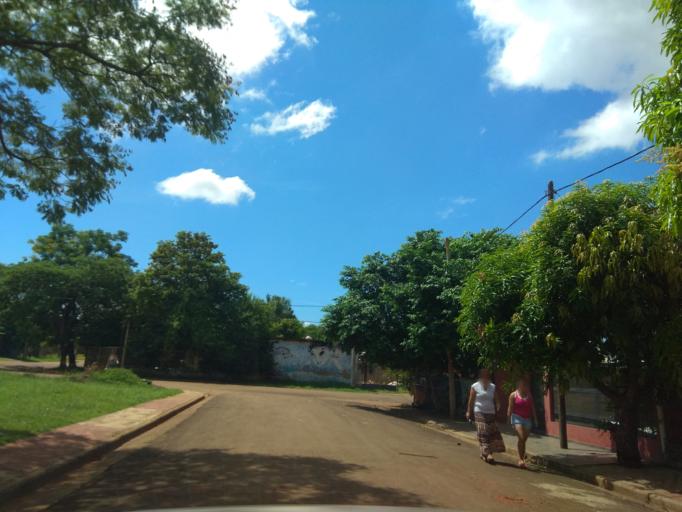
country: AR
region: Misiones
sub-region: Departamento de Capital
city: Posadas
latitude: -27.3861
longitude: -55.9240
